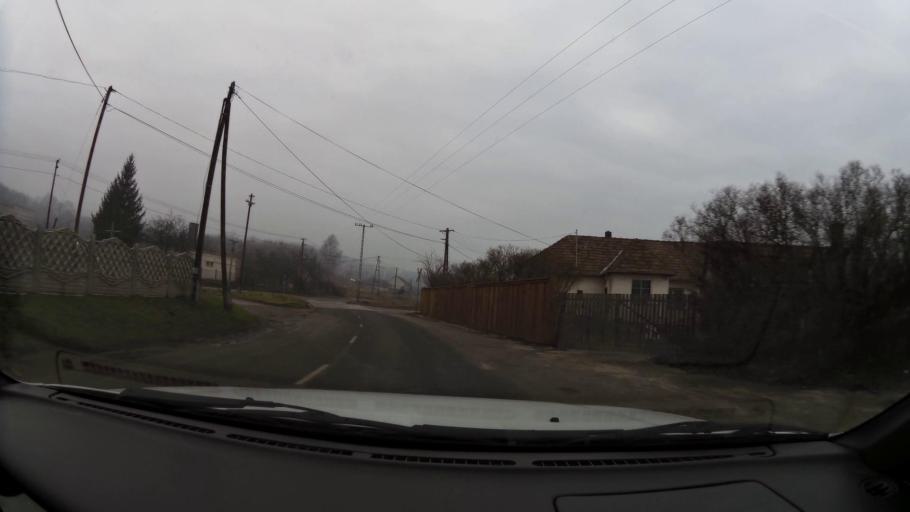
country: HU
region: Borsod-Abauj-Zemplen
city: Izsofalva
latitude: 48.3377
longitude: 20.6476
